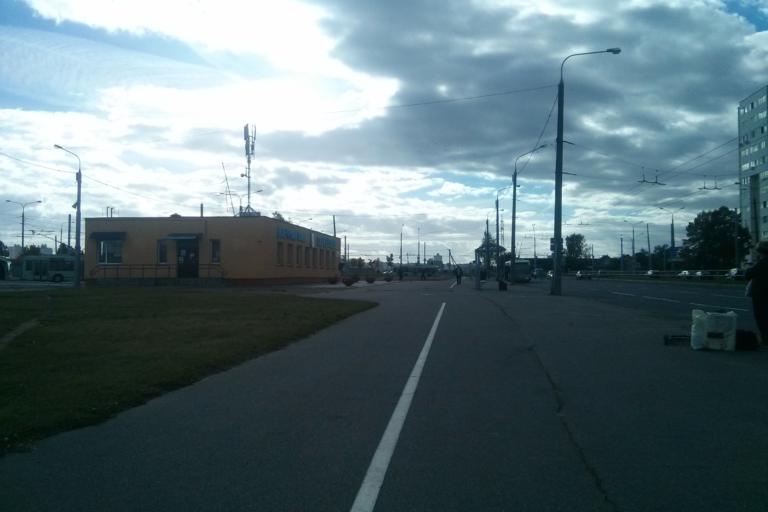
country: BY
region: Minsk
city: Minsk
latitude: 53.8490
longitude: 27.6035
